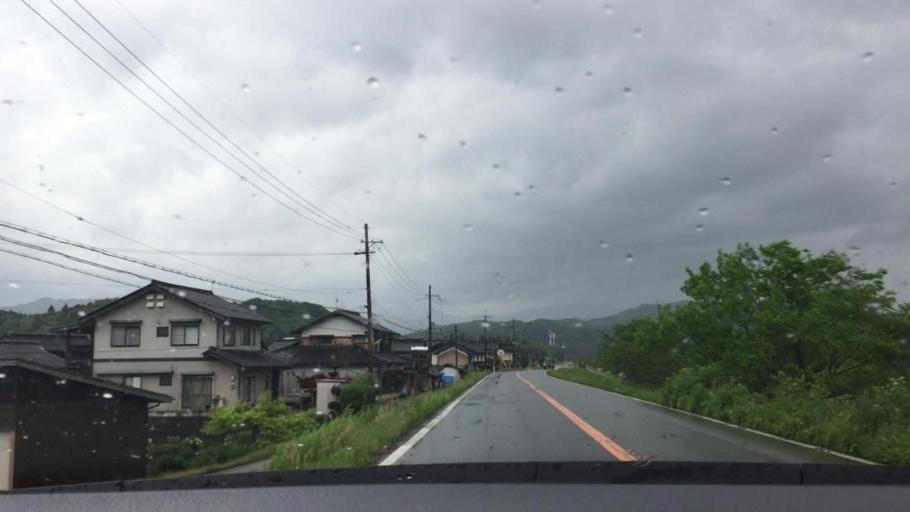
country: JP
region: Hyogo
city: Toyooka
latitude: 35.4798
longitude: 134.8019
